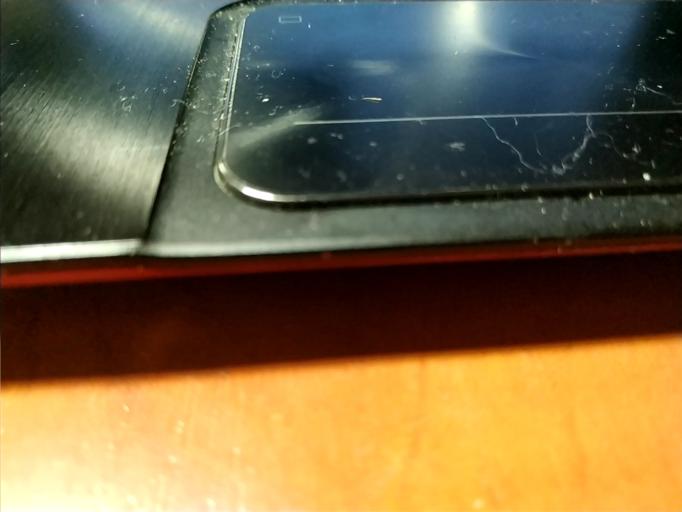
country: RU
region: Republic of Karelia
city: Kem'
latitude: 64.6555
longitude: 34.0799
